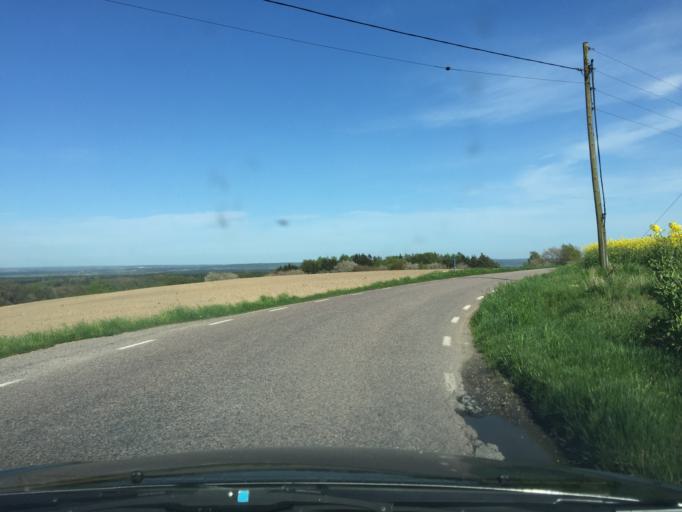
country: SE
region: Skane
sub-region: Sjobo Kommun
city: Blentarp
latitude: 55.5696
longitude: 13.5579
